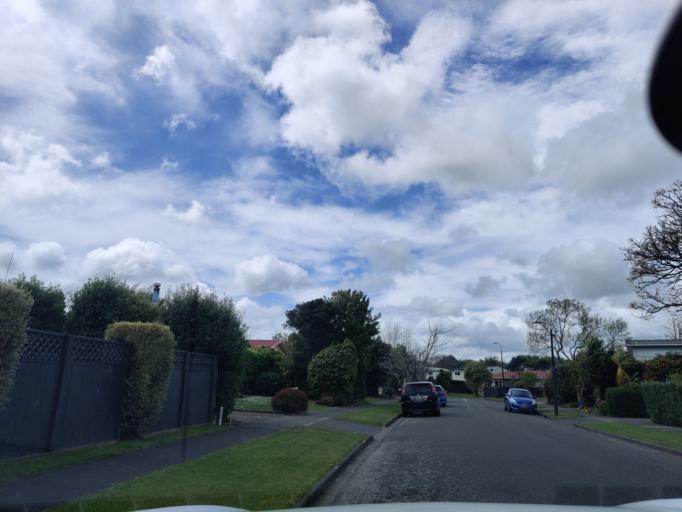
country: NZ
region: Manawatu-Wanganui
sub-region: Palmerston North City
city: Palmerston North
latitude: -40.3799
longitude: 175.5965
